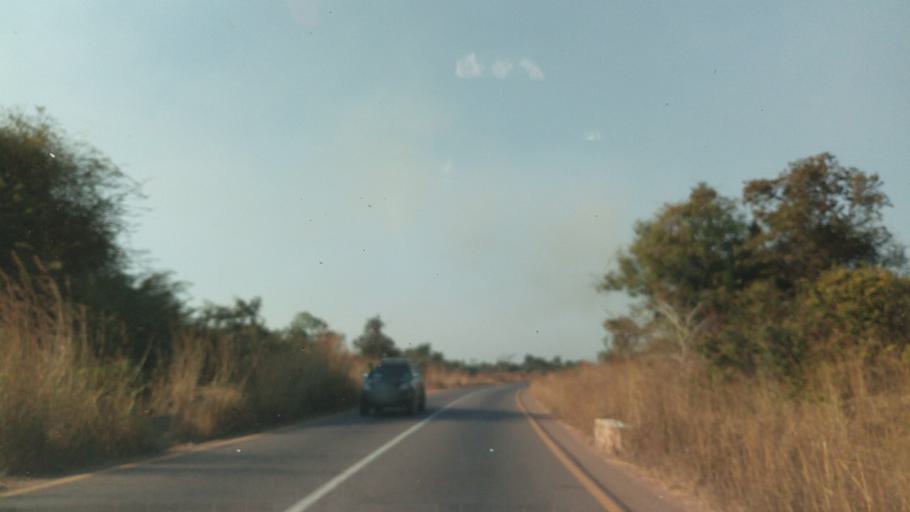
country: CD
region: Katanga
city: Lubumbashi
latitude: -11.4231
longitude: 27.7283
